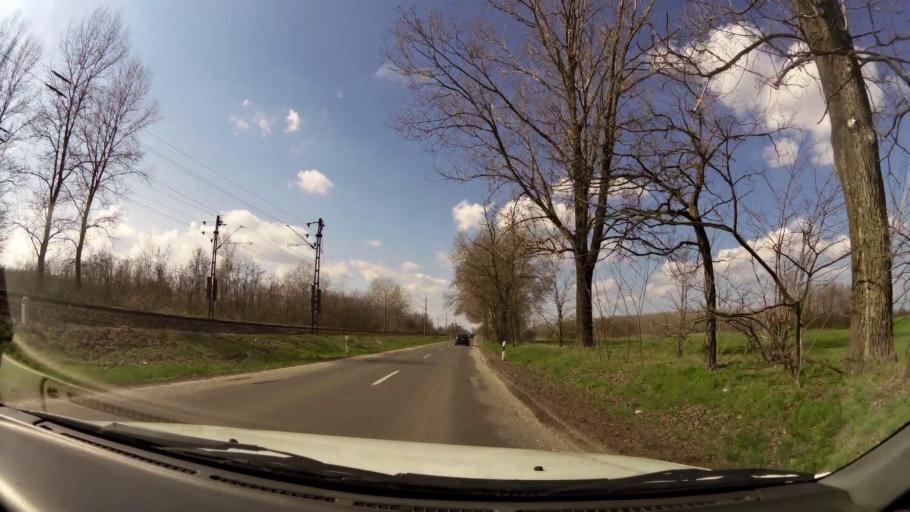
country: HU
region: Pest
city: Farmos
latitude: 47.3757
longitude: 19.7943
